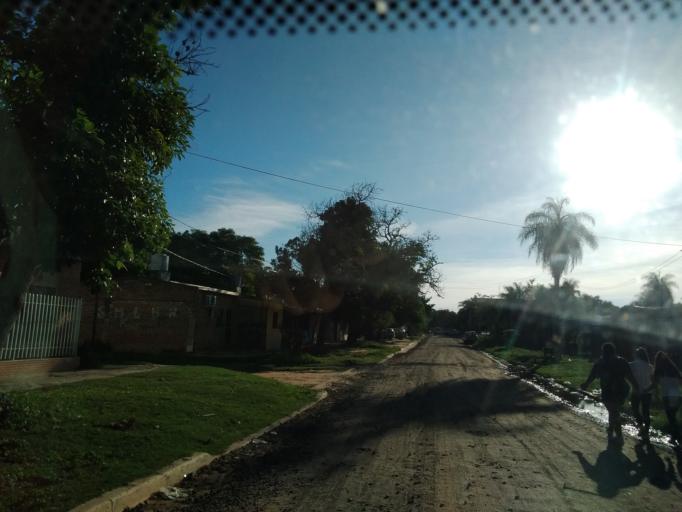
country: AR
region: Corrientes
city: Corrientes
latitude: -27.5067
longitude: -58.7945
